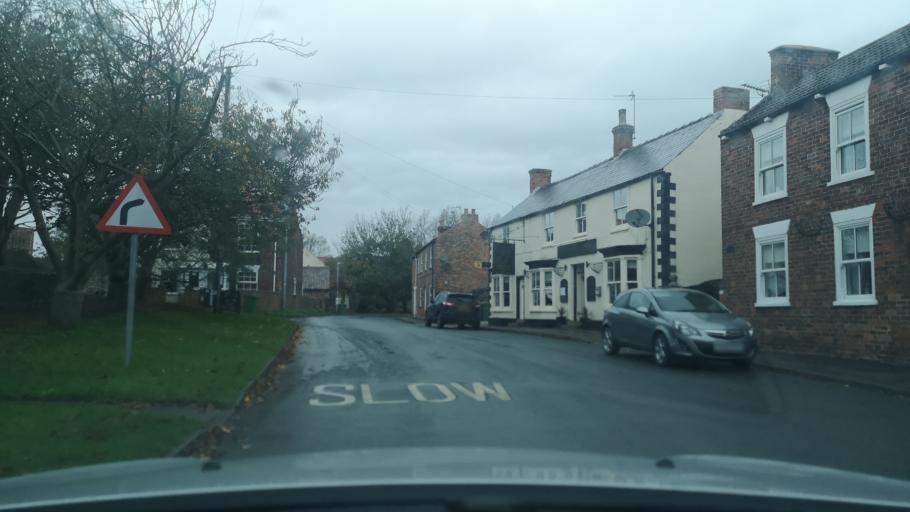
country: GB
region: England
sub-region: East Riding of Yorkshire
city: Easington
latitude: 53.6506
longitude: 0.1150
